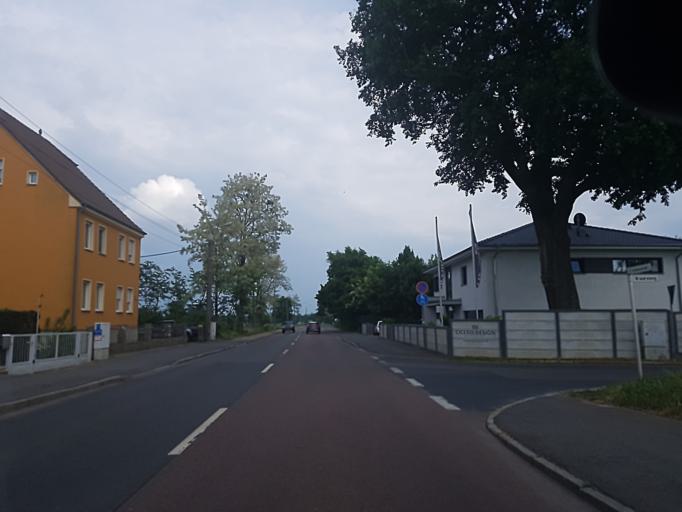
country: DE
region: Saxony-Anhalt
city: Wittenburg
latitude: 51.8754
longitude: 12.6111
